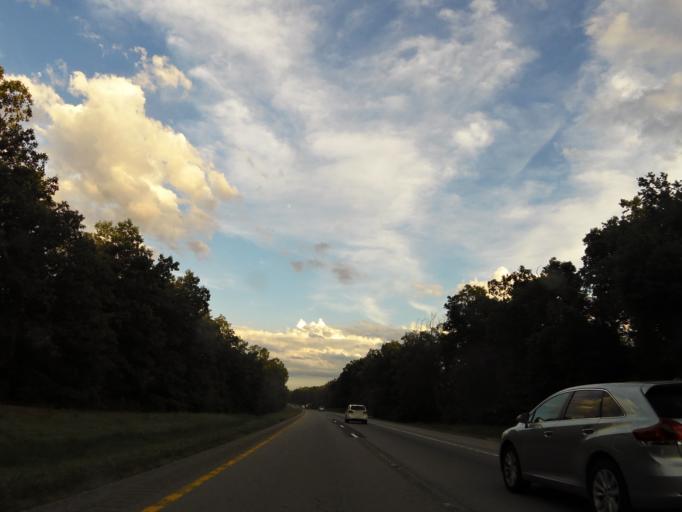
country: US
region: Tennessee
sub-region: Putnam County
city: Monterey
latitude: 36.0630
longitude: -85.1853
